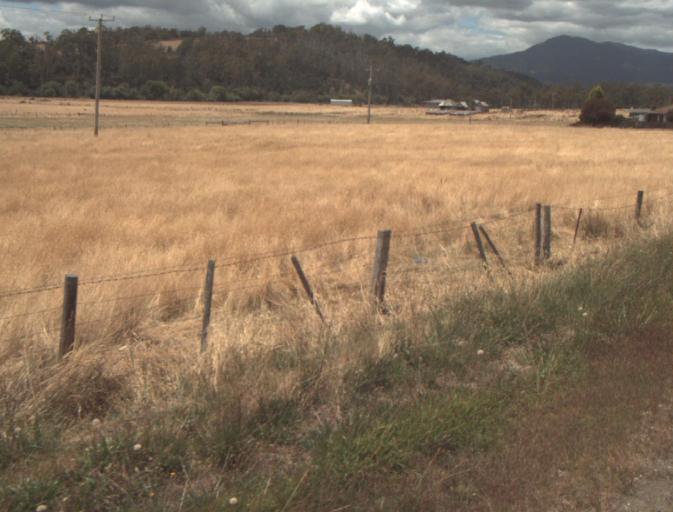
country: AU
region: Tasmania
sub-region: Launceston
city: Mayfield
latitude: -41.2247
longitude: 147.1378
